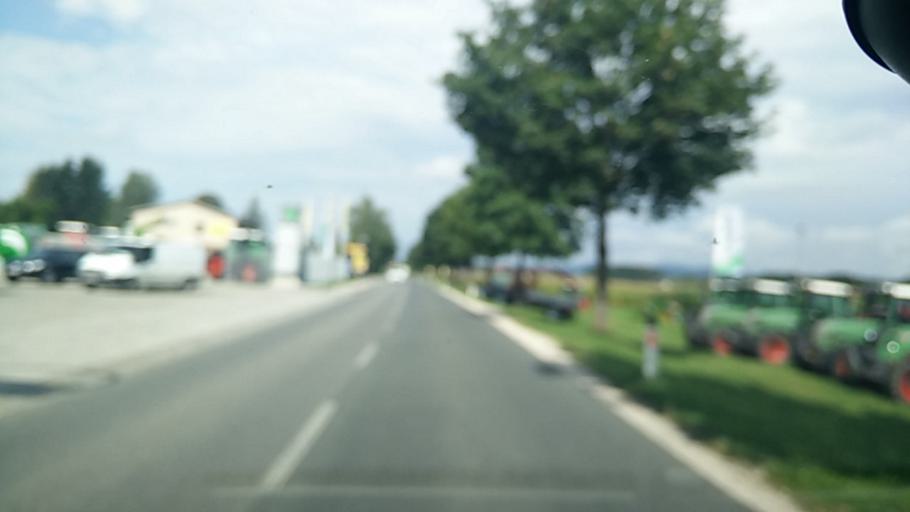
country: AT
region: Carinthia
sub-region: Politischer Bezirk Klagenfurt Land
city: Grafenstein
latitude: 46.6204
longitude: 14.4588
